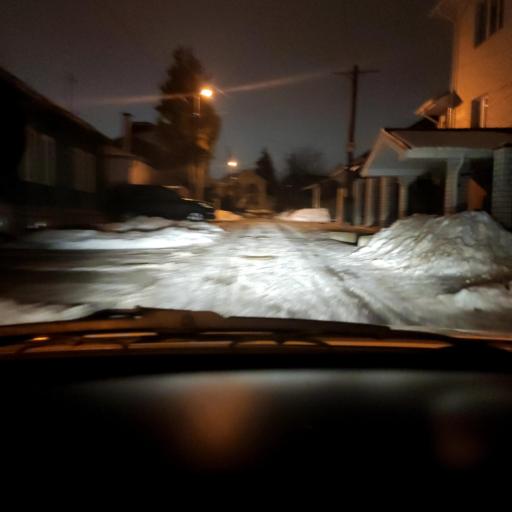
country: RU
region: Voronezj
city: Voronezh
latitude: 51.6981
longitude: 39.2118
